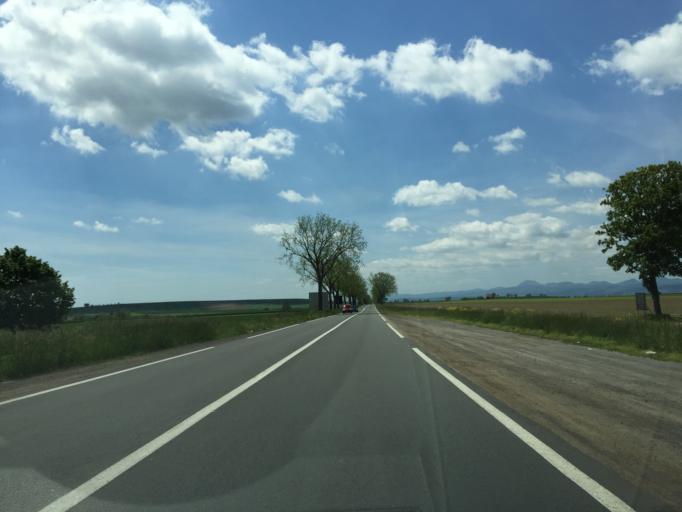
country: FR
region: Auvergne
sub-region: Departement du Puy-de-Dome
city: Aigueperse
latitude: 46.0085
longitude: 3.1969
